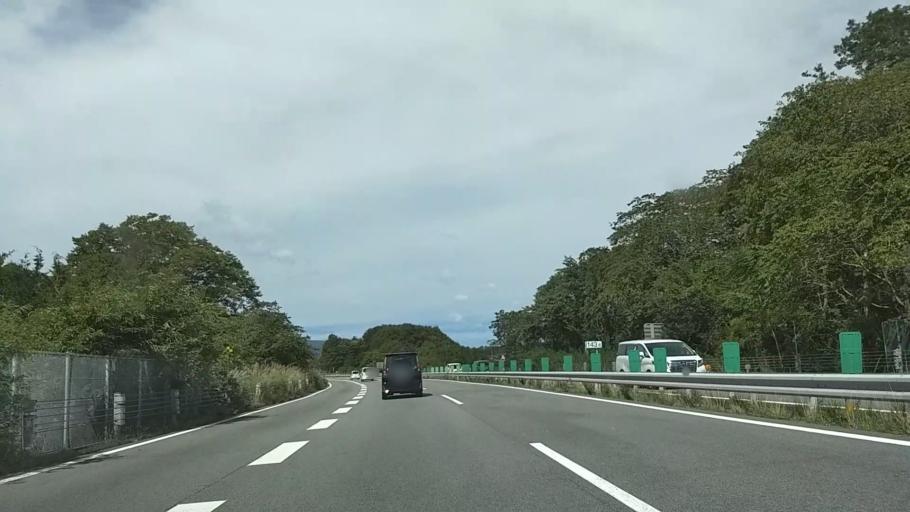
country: JP
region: Yamanashi
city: Nirasaki
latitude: 35.8498
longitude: 138.3554
